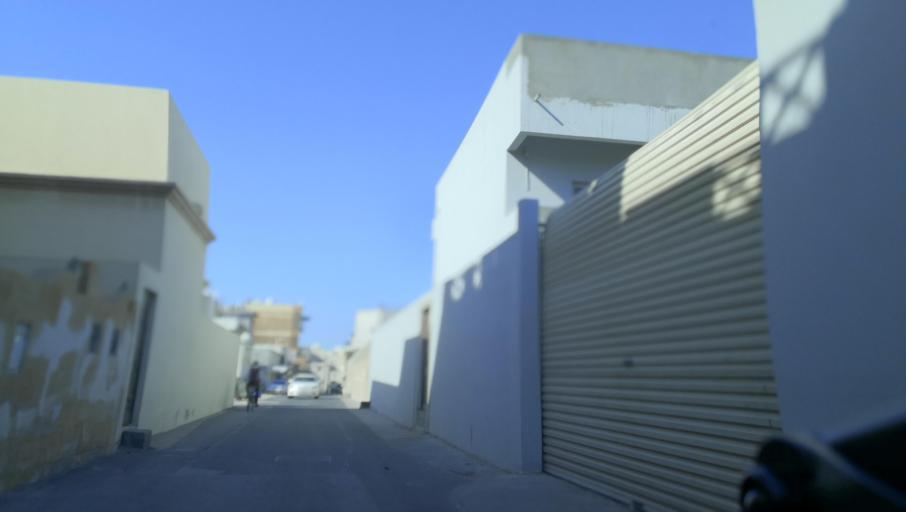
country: BH
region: Muharraq
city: Al Muharraq
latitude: 26.2545
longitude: 50.6338
